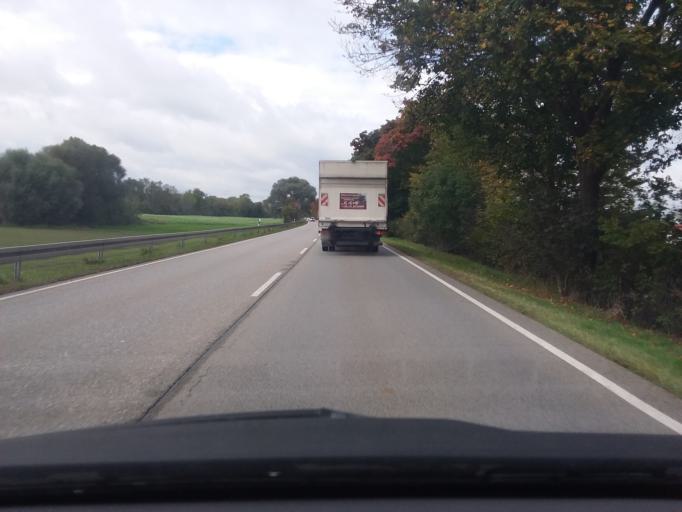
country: DE
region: Bavaria
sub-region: Upper Bavaria
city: Bergkirchen
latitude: 48.2393
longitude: 11.3643
